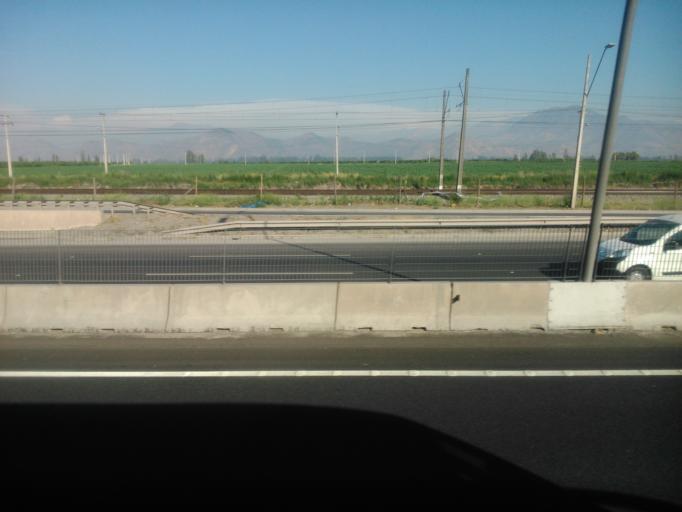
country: CL
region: Santiago Metropolitan
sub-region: Provincia de Maipo
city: Buin
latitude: -33.6683
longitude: -70.7209
